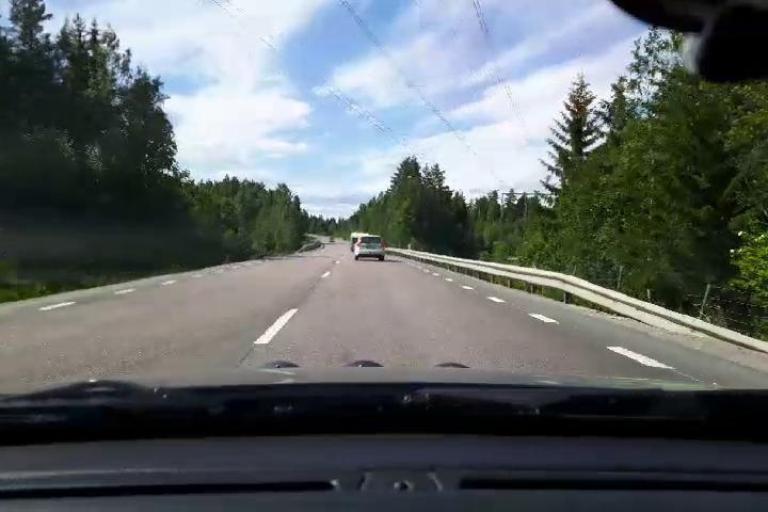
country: SE
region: Gaevleborg
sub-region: Bollnas Kommun
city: Kilafors
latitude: 61.2844
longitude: 16.5167
